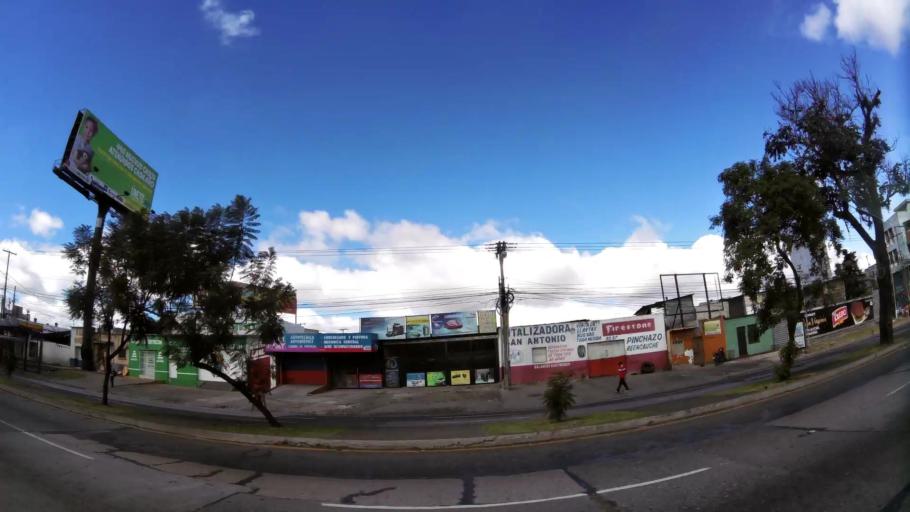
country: GT
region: Guatemala
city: Guatemala City
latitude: 14.6062
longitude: -90.5274
